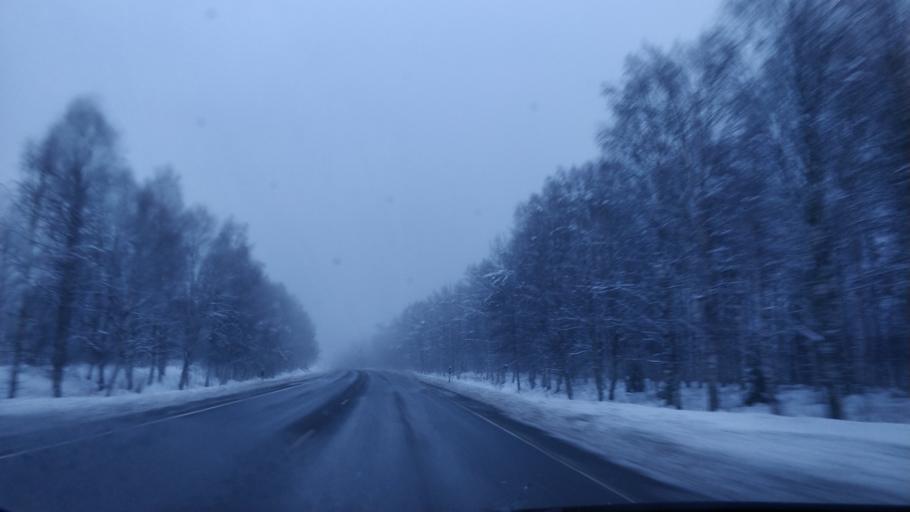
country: FI
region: Lapland
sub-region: Kemi-Tornio
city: Tervola
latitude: 66.1529
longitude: 25.0327
